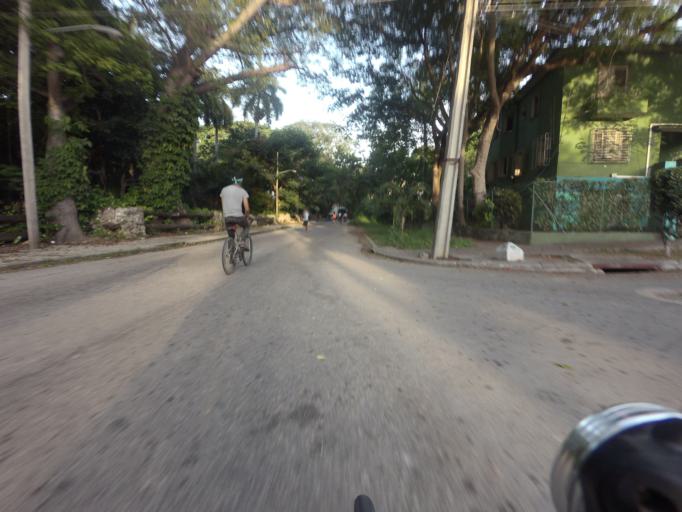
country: CU
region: La Habana
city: Havana
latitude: 23.1180
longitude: -82.4102
